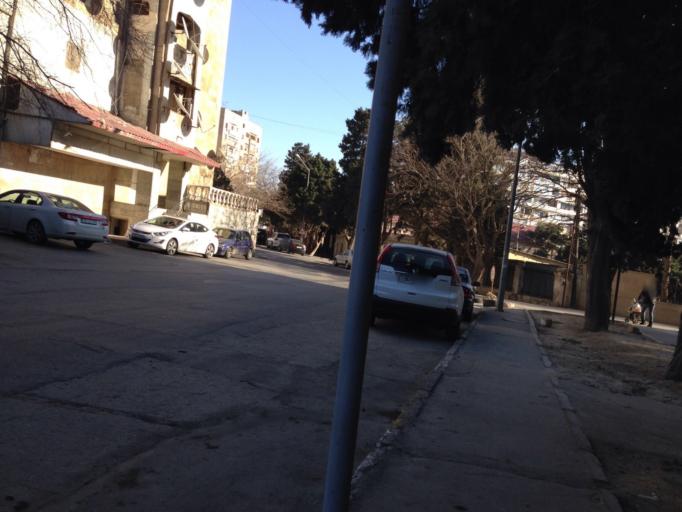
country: AZ
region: Baki
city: Baku
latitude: 40.3922
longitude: 49.8754
